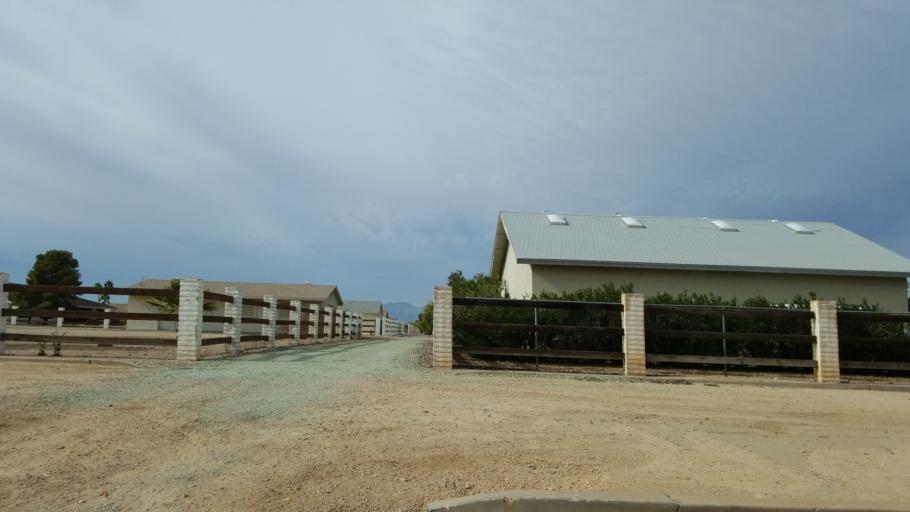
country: US
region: Arizona
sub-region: Maricopa County
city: Youngtown
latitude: 33.5777
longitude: -112.2988
